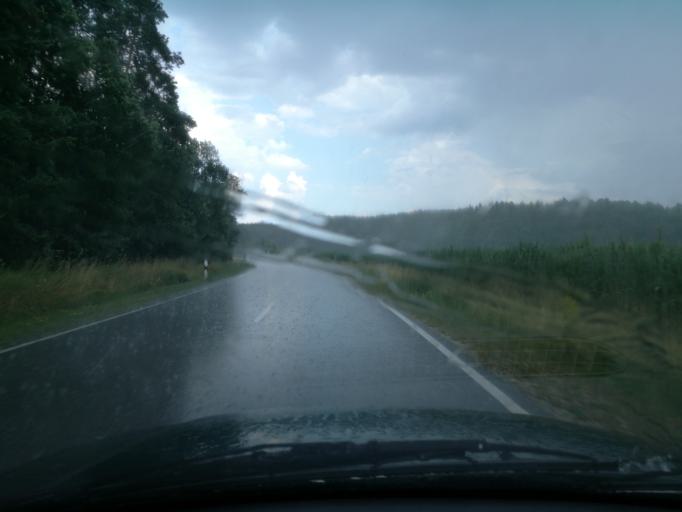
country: DE
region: Bavaria
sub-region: Regierungsbezirk Mittelfranken
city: Wilhermsdorf
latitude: 49.4495
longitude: 10.7457
